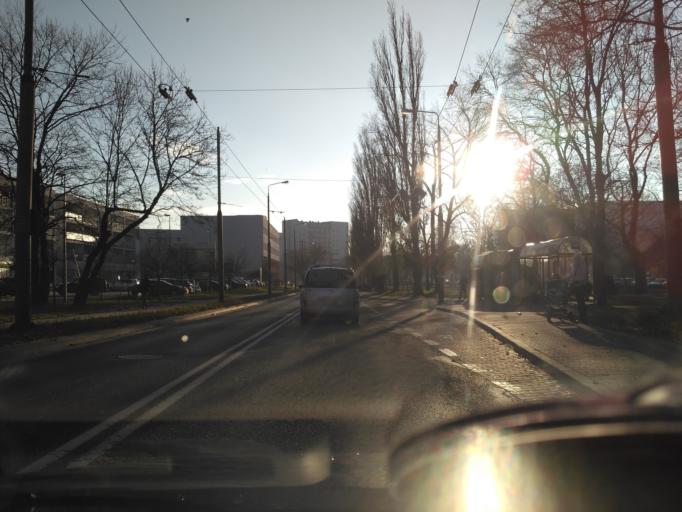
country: PL
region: Lublin Voivodeship
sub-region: Powiat lubelski
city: Lublin
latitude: 51.2605
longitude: 22.5654
